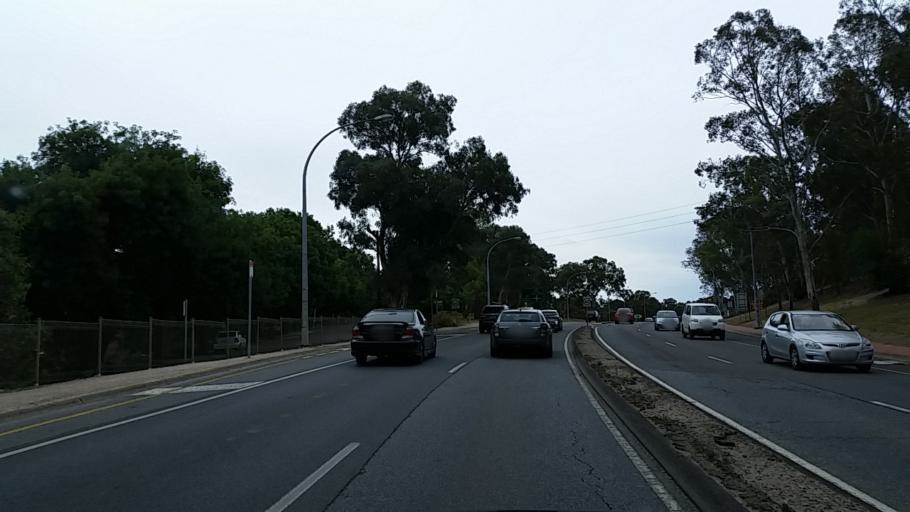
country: AU
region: South Australia
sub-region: Mount Barker
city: Little Hampton
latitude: -35.0613
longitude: 138.8527
